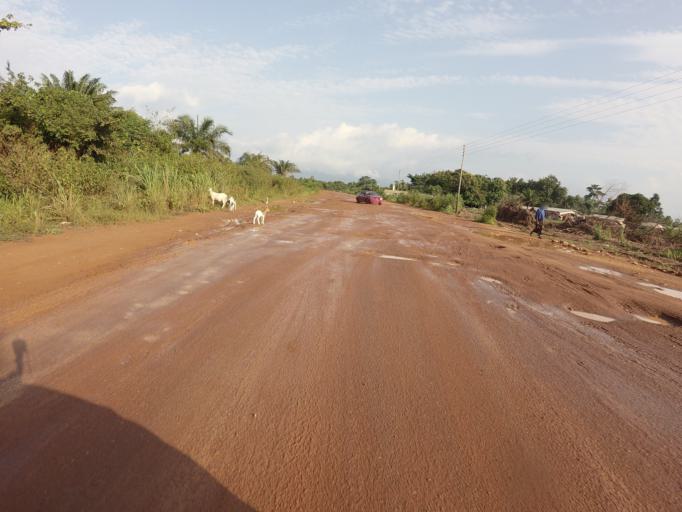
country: GH
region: Volta
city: Kpandu
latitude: 7.0093
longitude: 0.4290
